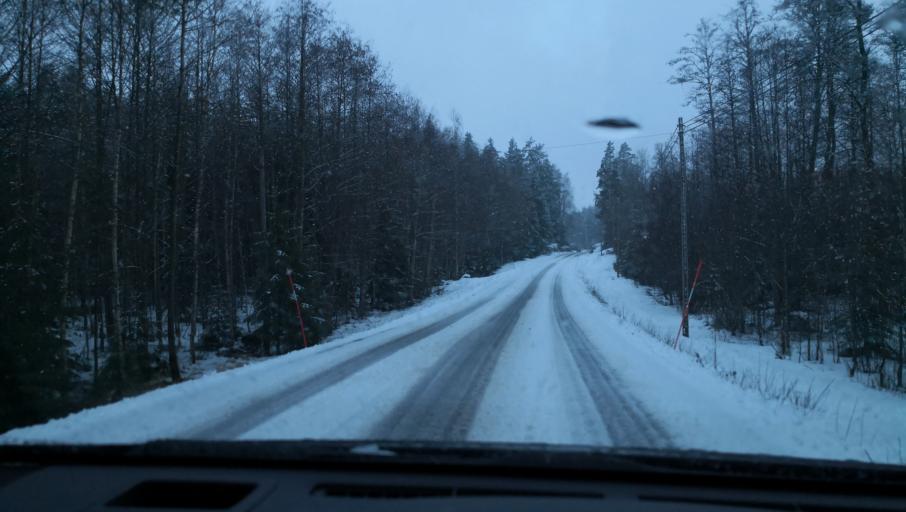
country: SE
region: Vaestmanland
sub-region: Kopings Kommun
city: Kolsva
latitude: 59.6036
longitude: 15.8641
